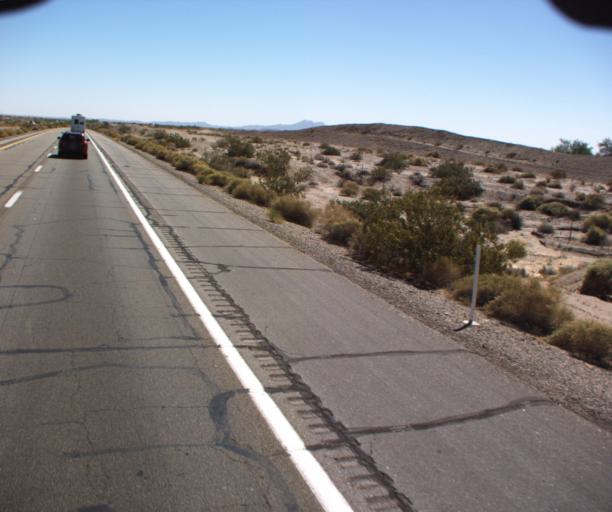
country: US
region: Arizona
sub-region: Yuma County
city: Wellton
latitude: 32.6541
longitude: -114.2317
